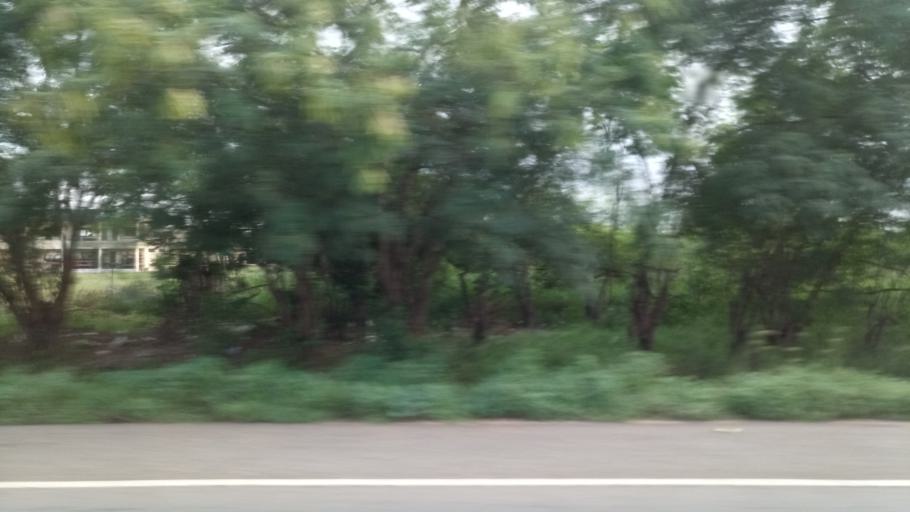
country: GH
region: Greater Accra
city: Tema
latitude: 5.8756
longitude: 0.3666
